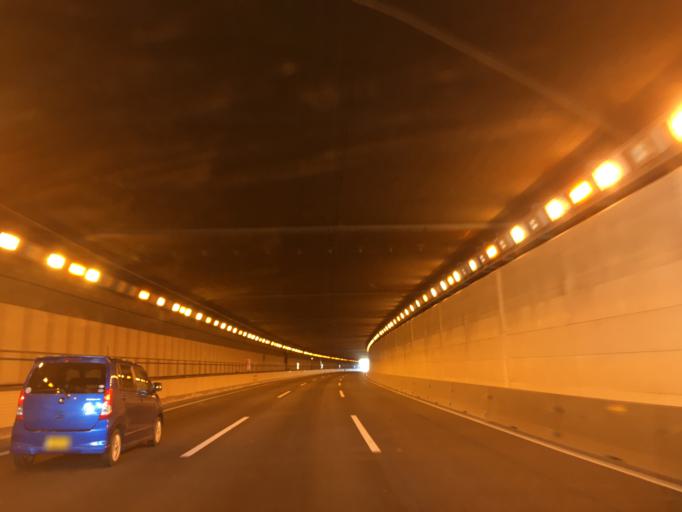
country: JP
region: Saitama
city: Wako
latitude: 35.7714
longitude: 139.6022
